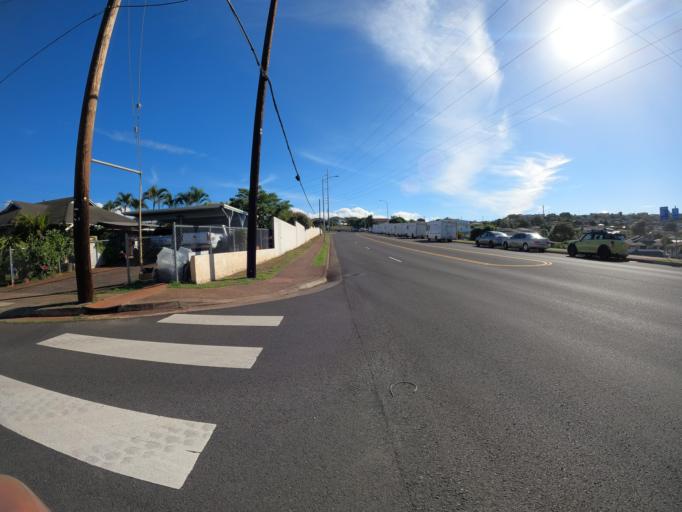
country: US
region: Hawaii
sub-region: Honolulu County
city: Halawa
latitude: 21.3586
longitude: -157.9250
